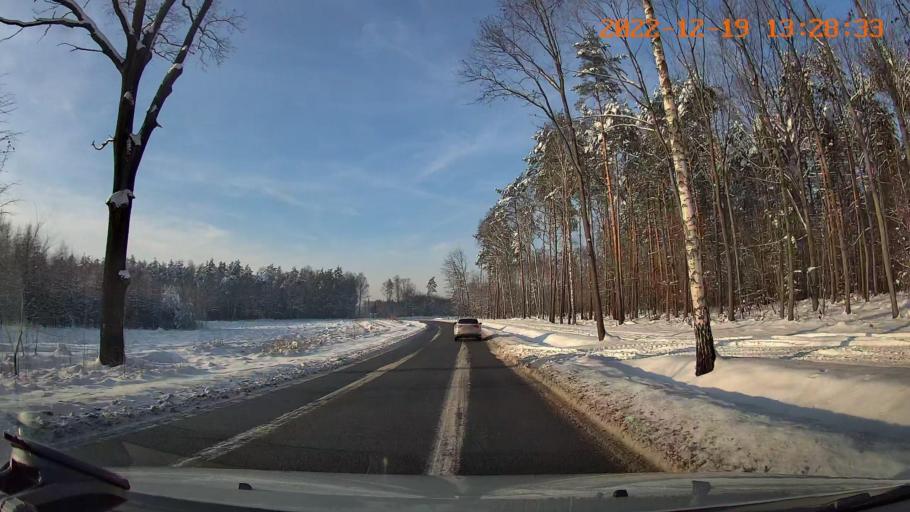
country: PL
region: Silesian Voivodeship
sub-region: Powiat bierunsko-ledzinski
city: Ledziny
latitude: 50.1124
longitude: 19.1267
